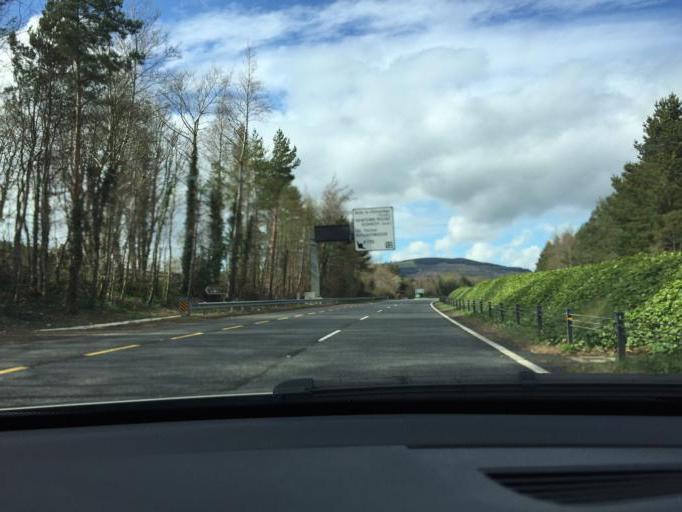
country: IE
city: Newtownmountkennedy
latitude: 53.0966
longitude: -6.1051
